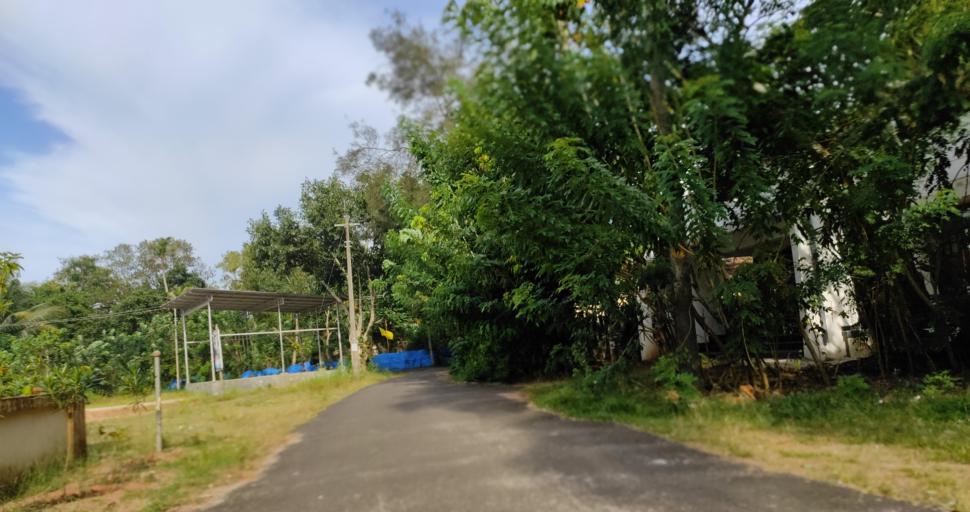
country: IN
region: Kerala
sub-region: Alappuzha
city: Shertallai
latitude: 9.6156
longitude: 76.3423
